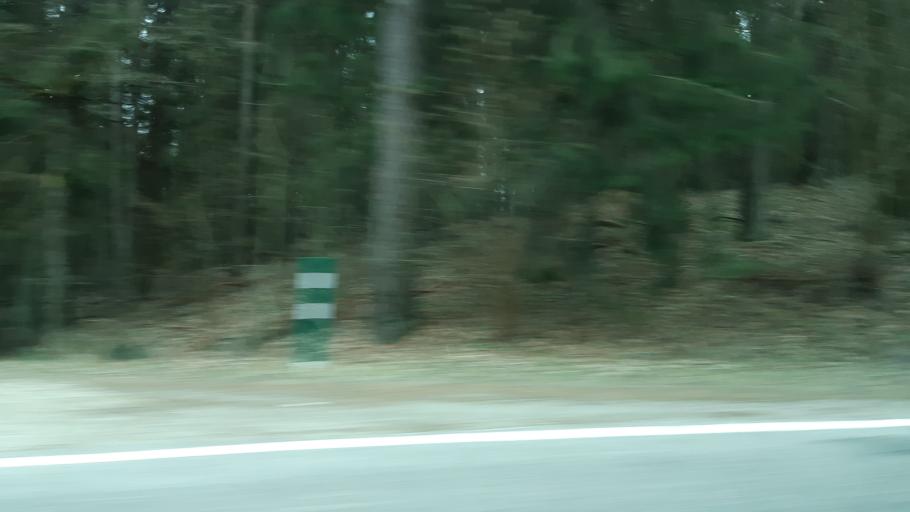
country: PL
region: Podlasie
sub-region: Suwalki
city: Suwalki
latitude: 54.3092
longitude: 22.9572
